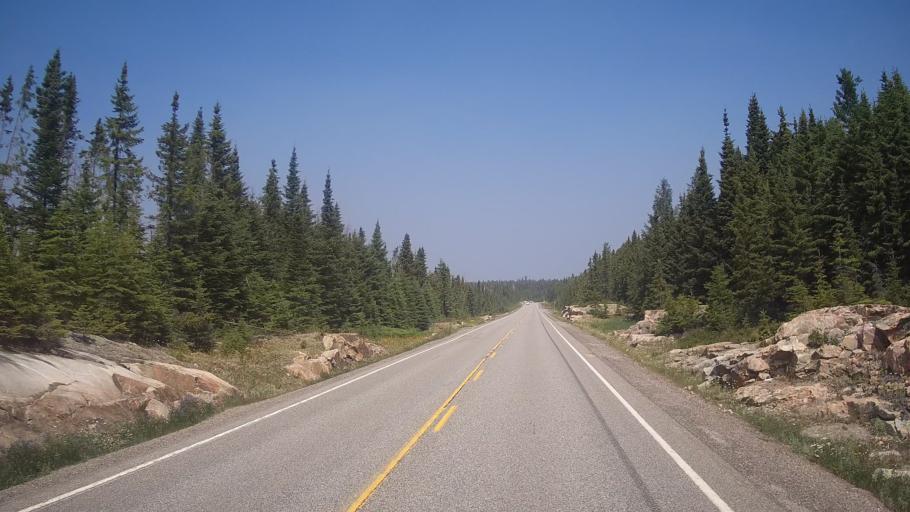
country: CA
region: Ontario
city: Timmins
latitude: 48.0694
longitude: -81.5902
